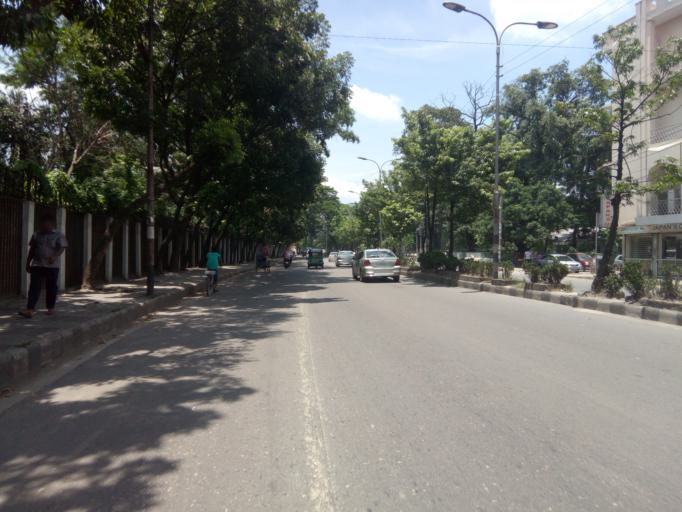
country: BD
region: Dhaka
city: Paltan
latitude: 23.7390
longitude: 90.4054
